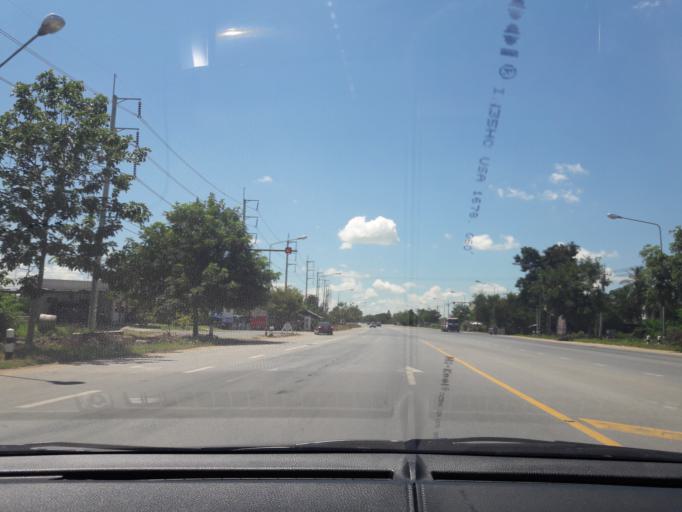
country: TH
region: Kanchanaburi
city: Tha Maka
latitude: 14.0345
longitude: 99.8184
